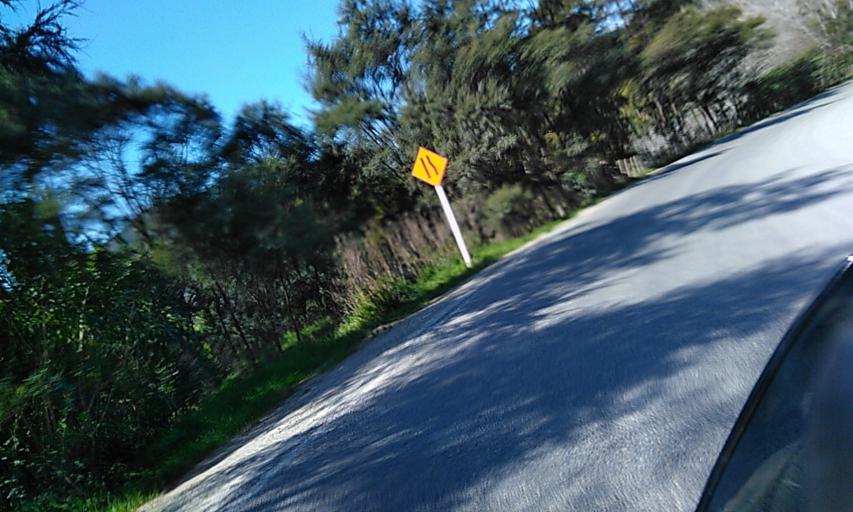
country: NZ
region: Gisborne
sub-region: Gisborne District
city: Gisborne
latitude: -38.3189
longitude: 178.1431
